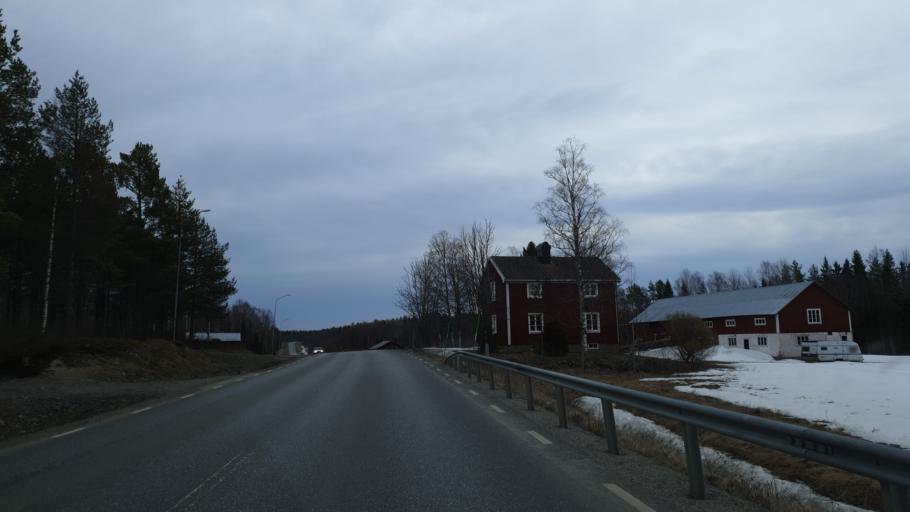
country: SE
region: Vaesterbotten
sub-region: Robertsfors Kommun
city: Robertsfors
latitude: 64.2321
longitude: 20.9961
